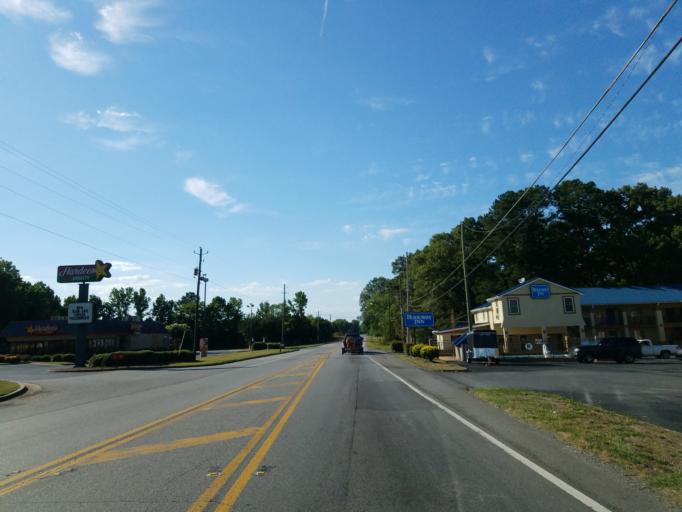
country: US
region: Georgia
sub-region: Gordon County
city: Calhoun
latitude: 34.5599
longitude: -84.9368
